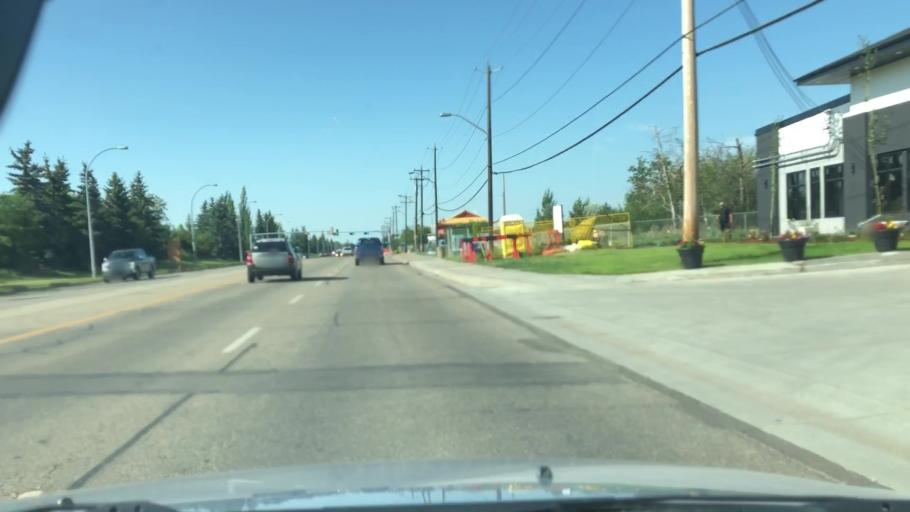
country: CA
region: Alberta
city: Edmonton
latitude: 53.6086
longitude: -113.5412
